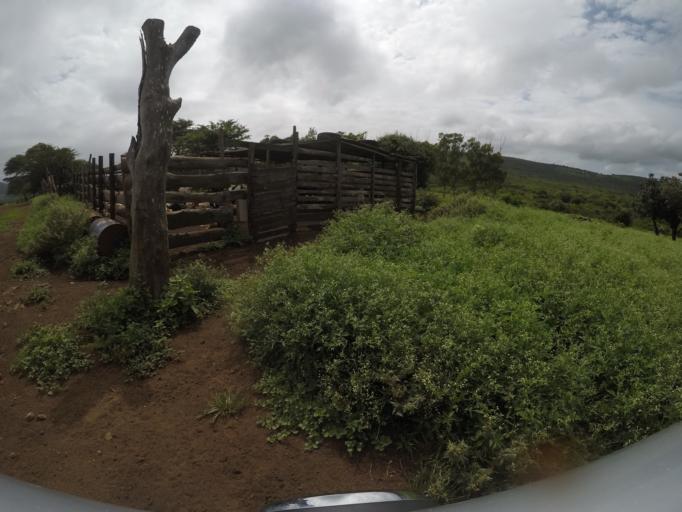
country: ZA
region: KwaZulu-Natal
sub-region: uThungulu District Municipality
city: Empangeni
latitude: -28.6203
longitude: 31.8743
